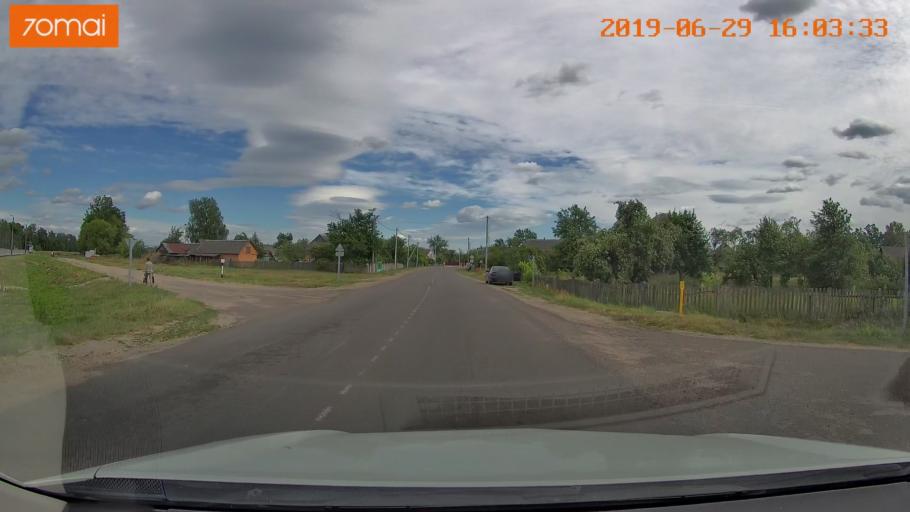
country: BY
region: Brest
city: Luninyets
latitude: 52.2289
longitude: 27.0200
